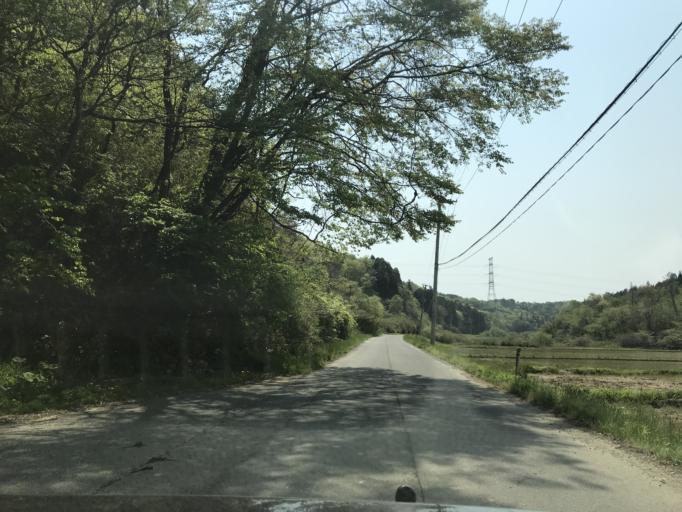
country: JP
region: Iwate
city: Ichinoseki
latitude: 38.8472
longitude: 141.0664
